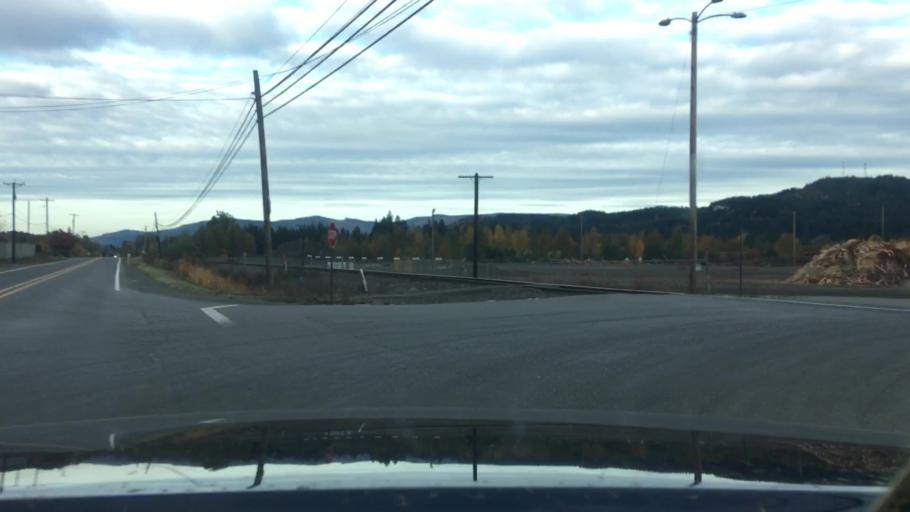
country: US
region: Oregon
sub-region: Lane County
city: Cottage Grove
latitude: 43.7696
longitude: -123.0796
